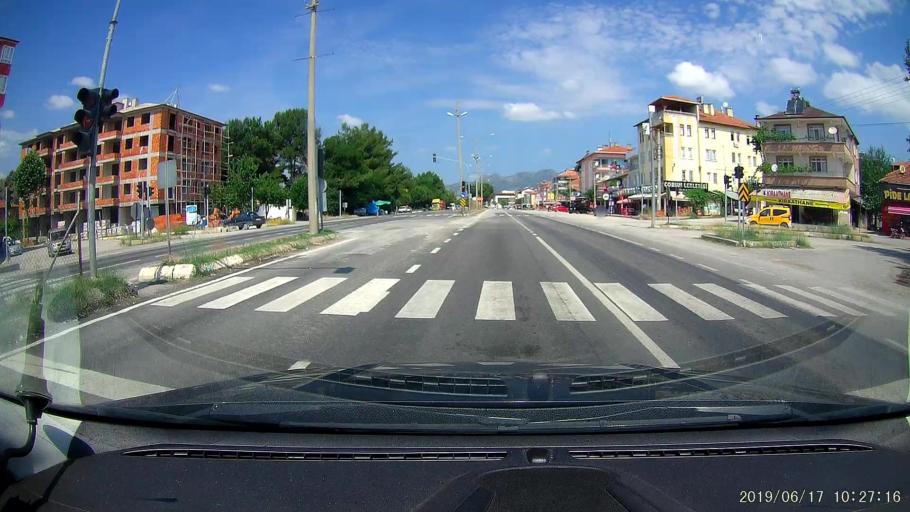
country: TR
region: Corum
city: Osmancik
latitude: 40.9764
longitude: 34.8120
